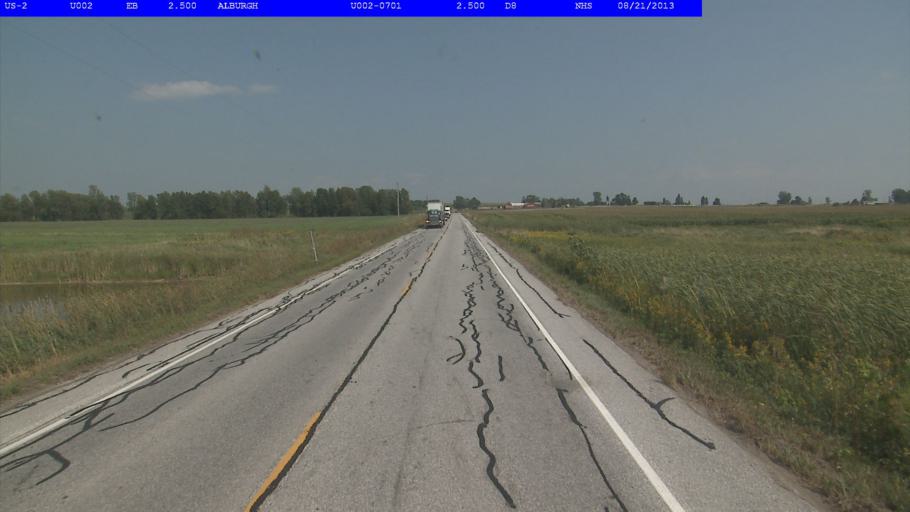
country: US
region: New York
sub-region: Clinton County
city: Rouses Point
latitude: 44.9911
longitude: -73.3075
